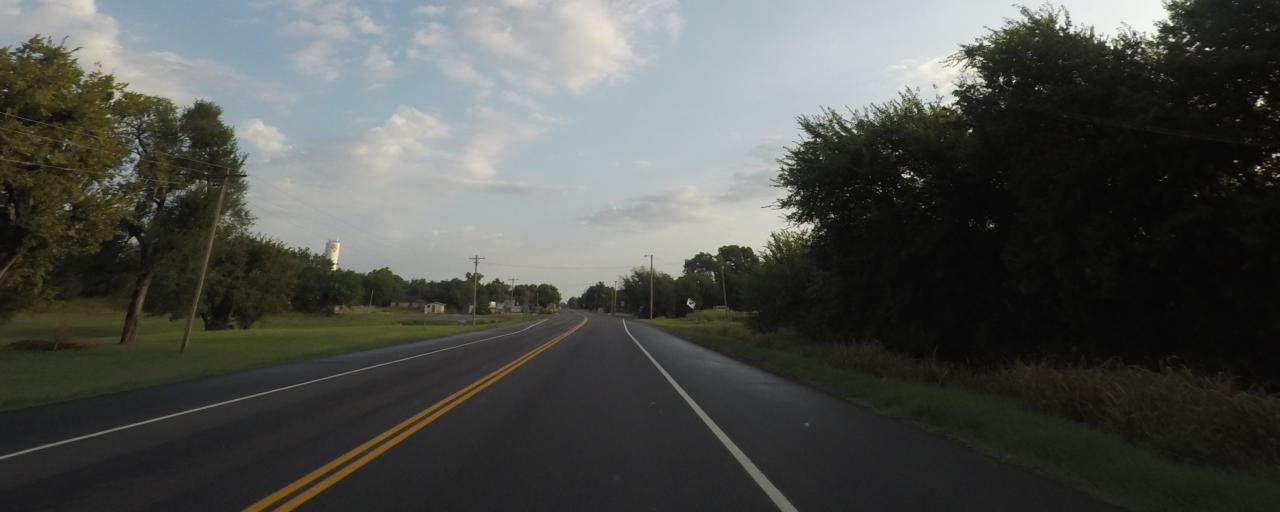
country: US
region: Oklahoma
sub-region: Stephens County
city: Comanche
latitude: 34.3605
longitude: -97.9644
